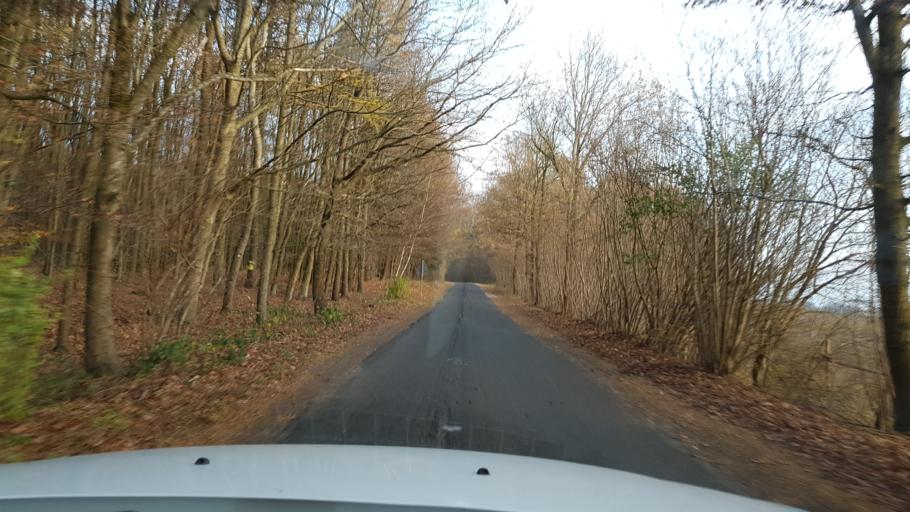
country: PL
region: West Pomeranian Voivodeship
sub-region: Koszalin
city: Koszalin
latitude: 54.1045
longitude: 16.1384
